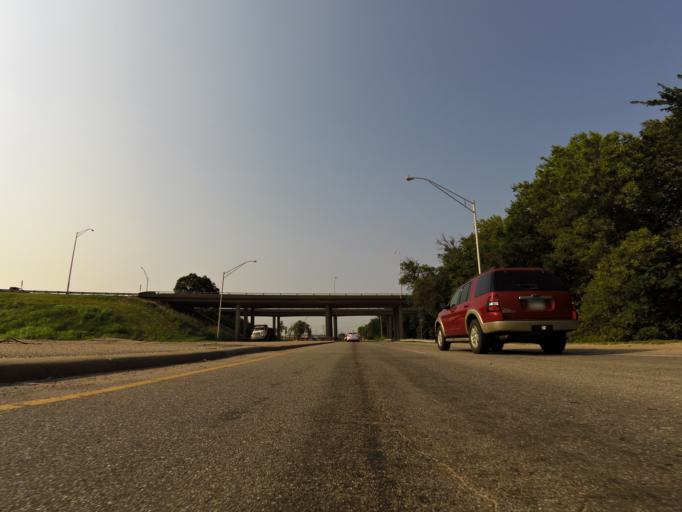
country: US
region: Kansas
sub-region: Sedgwick County
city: Park City
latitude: 37.7565
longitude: -97.3362
